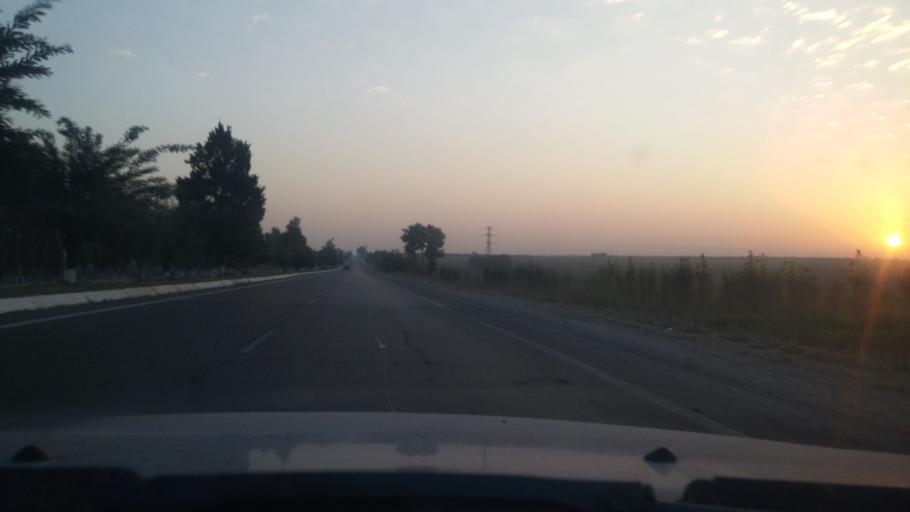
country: UZ
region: Toshkent
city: Zafar
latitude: 41.0183
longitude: 68.8497
